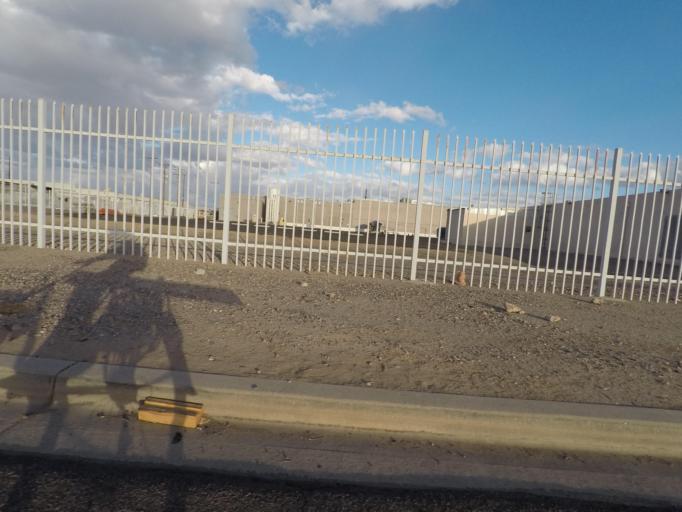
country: US
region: Arizona
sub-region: Maricopa County
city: Glendale
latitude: 33.4990
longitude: -112.1447
